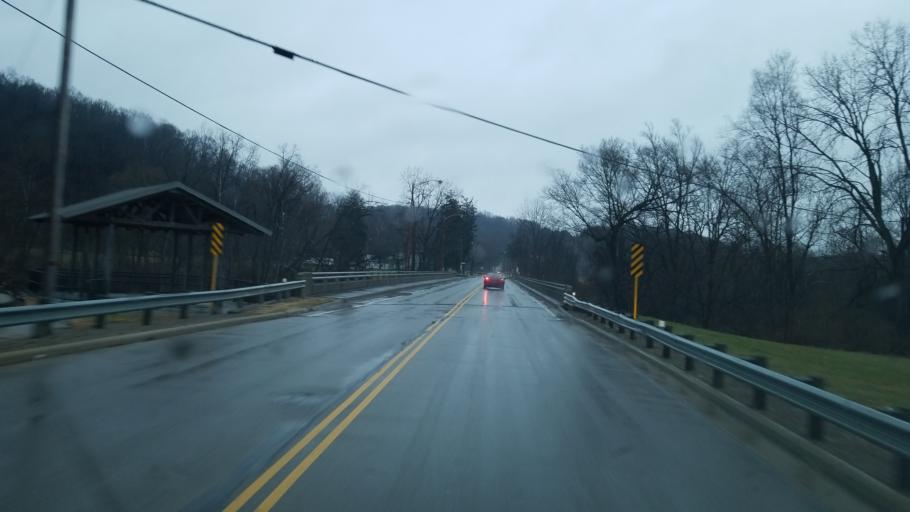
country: US
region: Ohio
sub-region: Licking County
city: Newark
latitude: 40.0870
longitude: -82.4115
